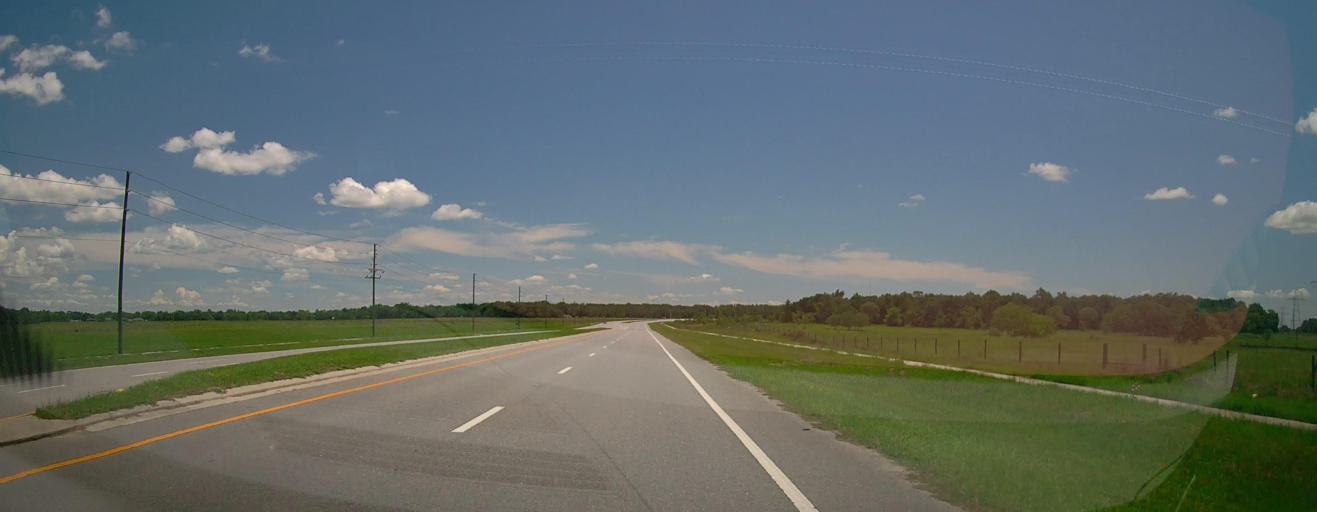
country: US
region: Florida
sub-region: Marion County
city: Silver Springs Shores
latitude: 29.0691
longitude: -82.0238
